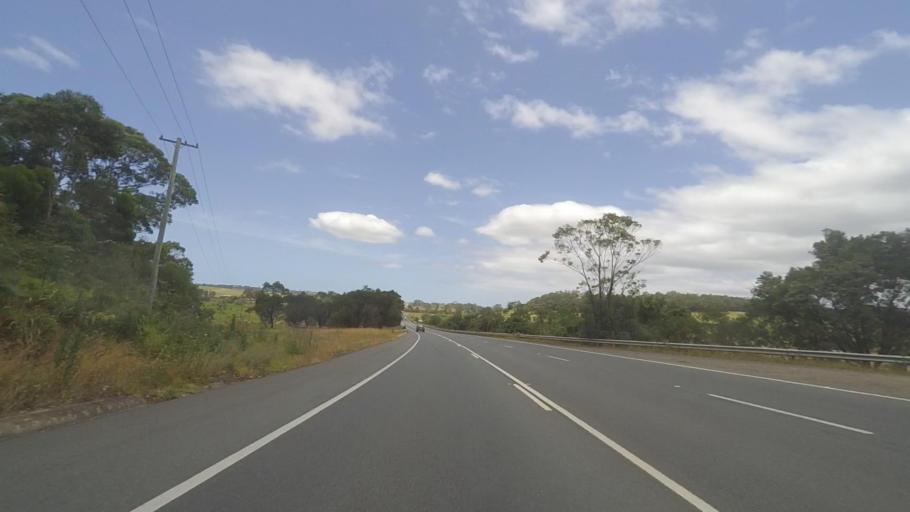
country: AU
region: New South Wales
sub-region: Shoalhaven Shire
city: Milton
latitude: -35.2658
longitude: 150.4249
